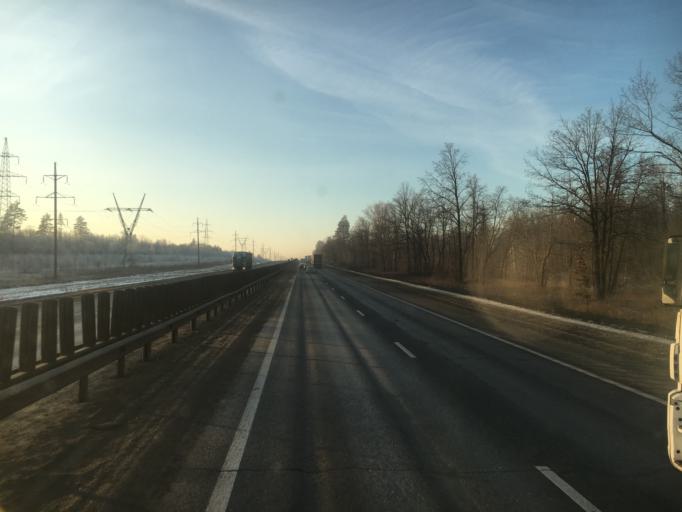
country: RU
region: Samara
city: Pribrezhnyy
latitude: 53.5153
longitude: 49.8767
